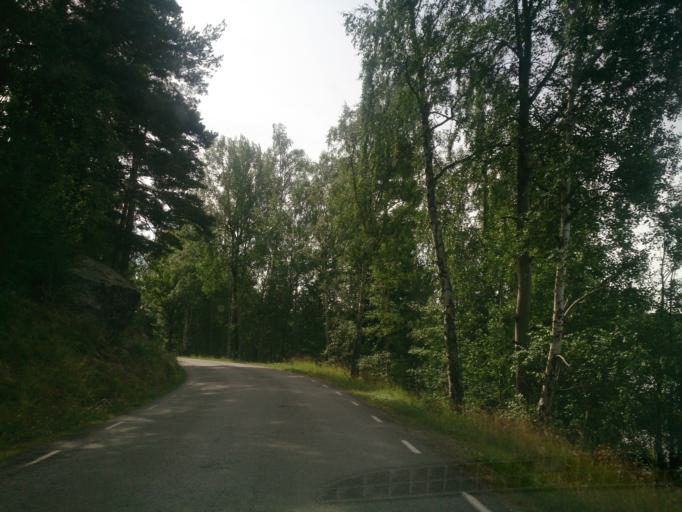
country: SE
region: OEstergoetland
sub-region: Atvidabergs Kommun
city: Atvidaberg
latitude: 58.3118
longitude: 16.0667
